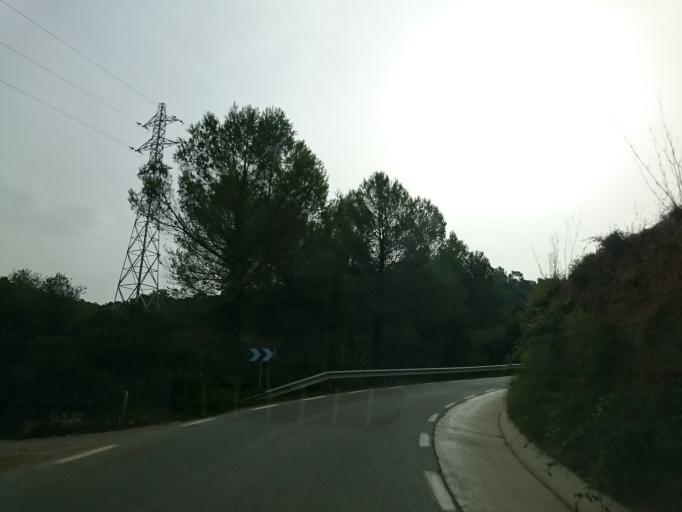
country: ES
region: Catalonia
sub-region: Provincia de Barcelona
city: Olivella
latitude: 41.3127
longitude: 1.8063
